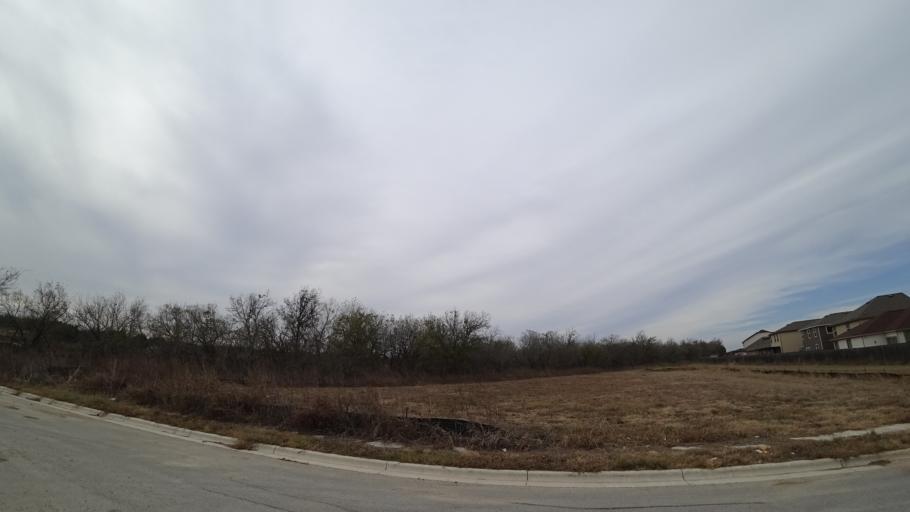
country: US
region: Texas
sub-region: Travis County
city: Onion Creek
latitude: 30.1464
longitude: -97.7416
